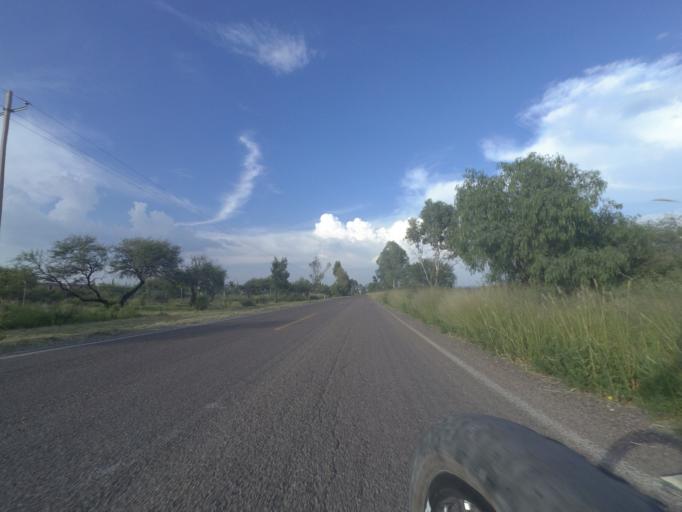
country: MX
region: Aguascalientes
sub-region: Aguascalientes
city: Penuelas (El Cienegal)
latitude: 21.7170
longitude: -102.3686
